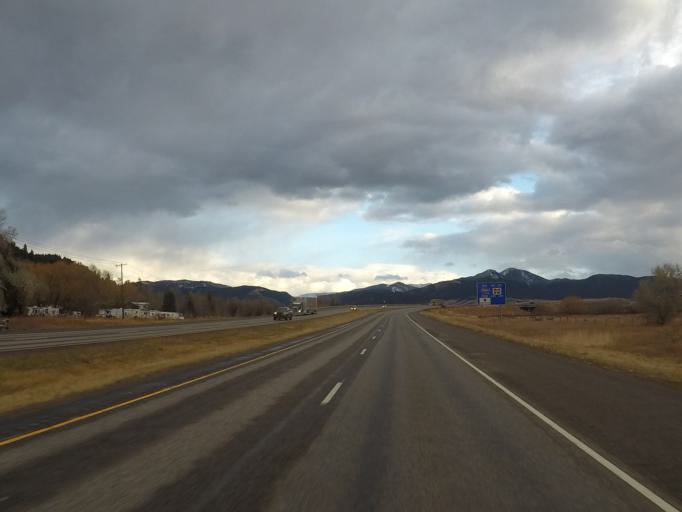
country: US
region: Montana
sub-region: Gallatin County
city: Bozeman
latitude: 45.6842
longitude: -111.0145
